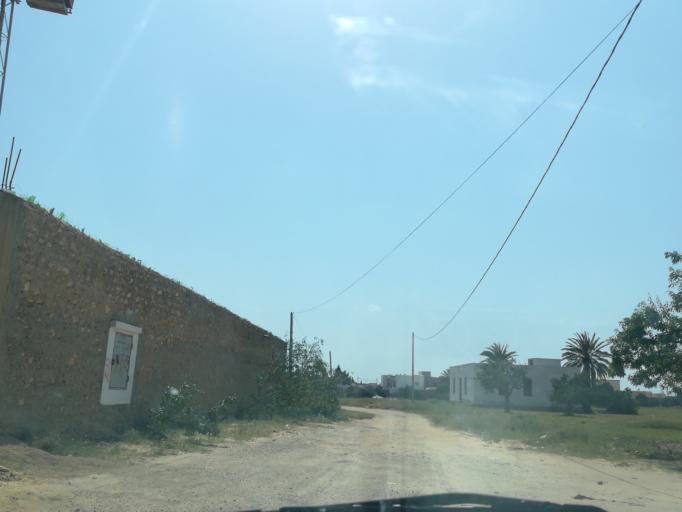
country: TN
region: Safaqis
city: Al Qarmadah
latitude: 34.8221
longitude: 10.7621
